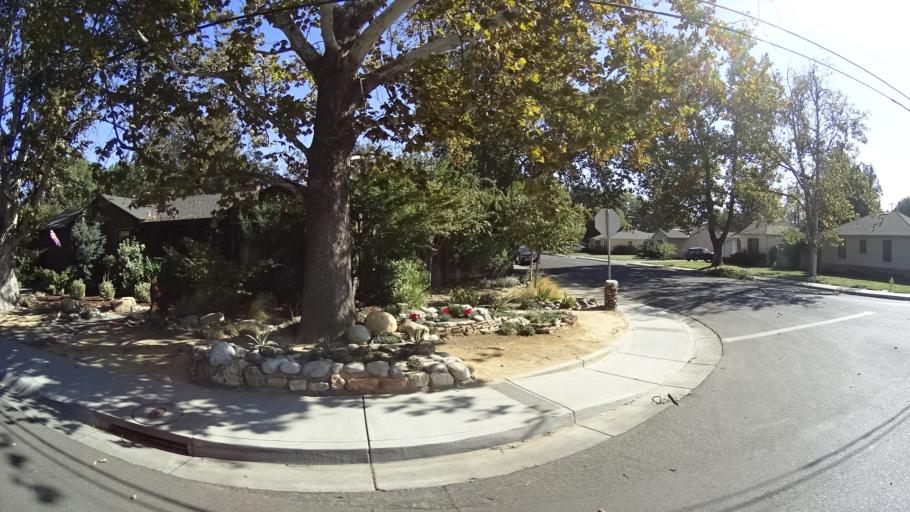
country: US
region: California
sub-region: Yolo County
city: Woodland
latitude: 38.6650
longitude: -121.7841
